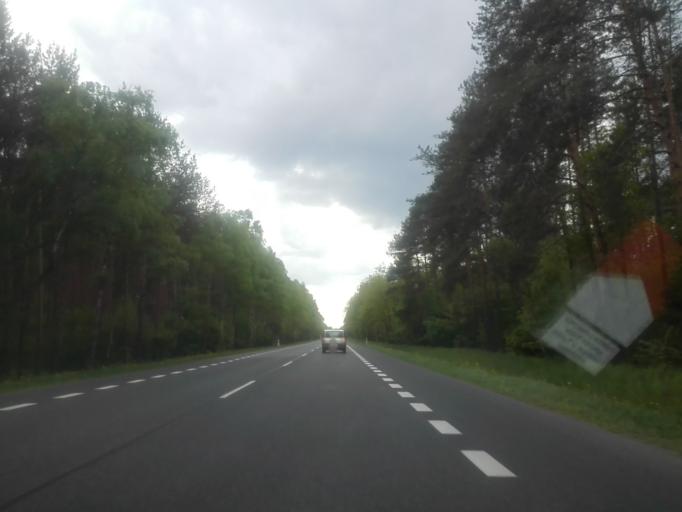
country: PL
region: Masovian Voivodeship
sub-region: Powiat ostrowski
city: Ostrow Mazowiecka
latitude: 52.8508
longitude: 21.9826
